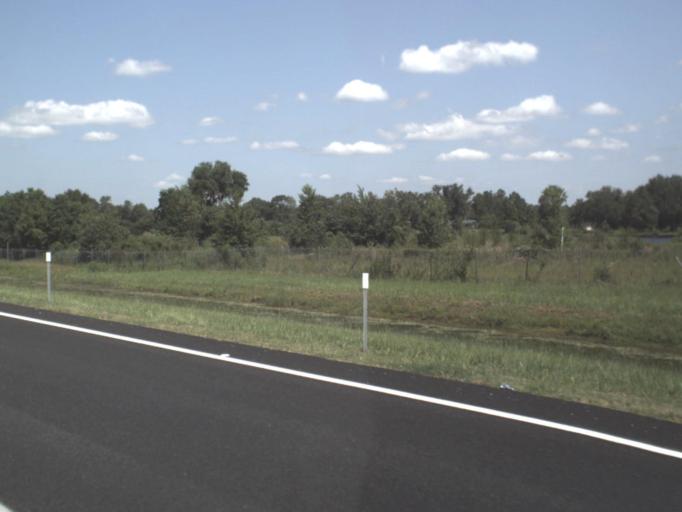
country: US
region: Florida
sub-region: Madison County
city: Madison
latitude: 30.3966
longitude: -83.3618
